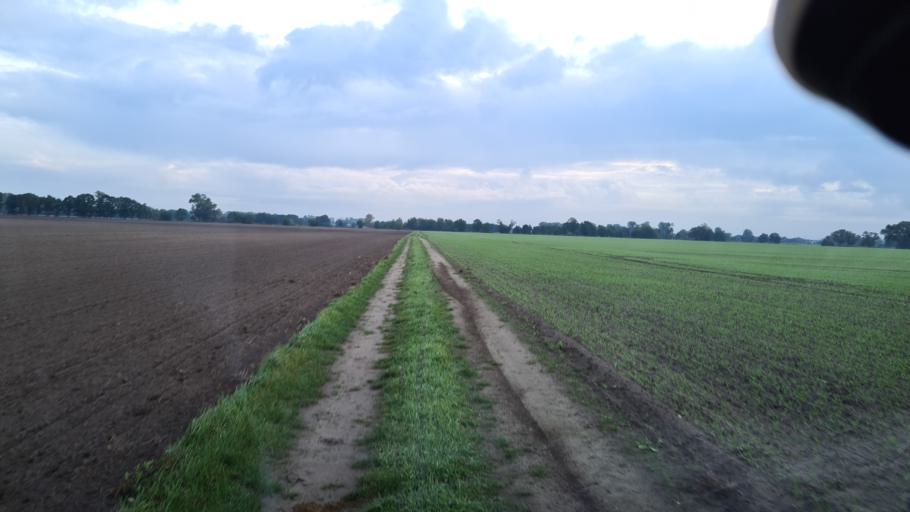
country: DE
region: Brandenburg
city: Schonewalde
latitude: 51.6820
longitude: 13.5712
